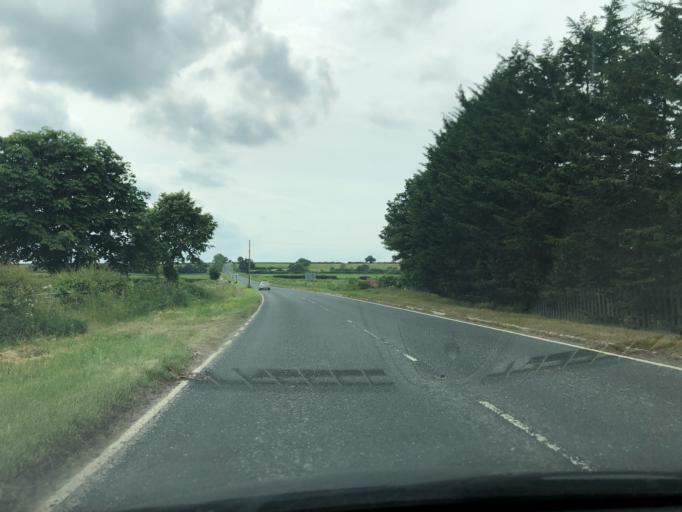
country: GB
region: England
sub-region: North Yorkshire
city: Pickering
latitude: 54.2628
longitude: -0.8298
